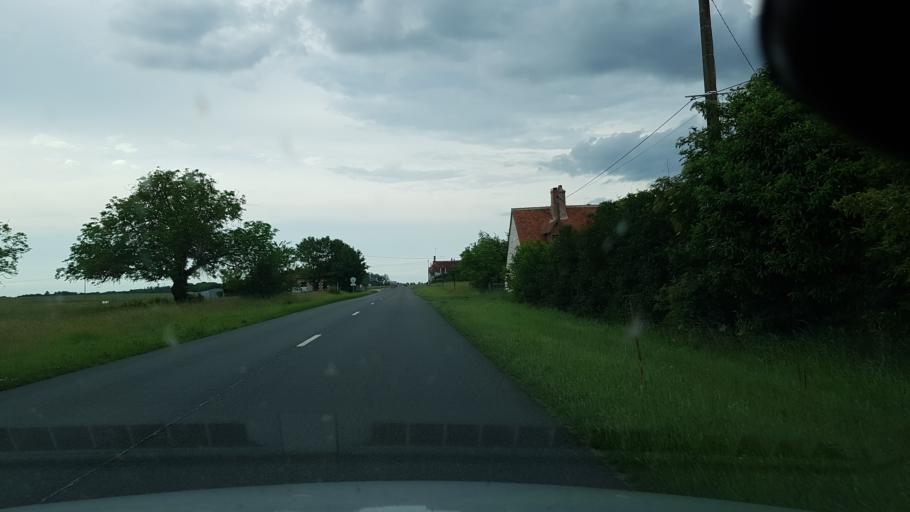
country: FR
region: Centre
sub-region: Departement du Loir-et-Cher
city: Chatillon-sur-Cher
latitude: 47.3080
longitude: 1.5060
